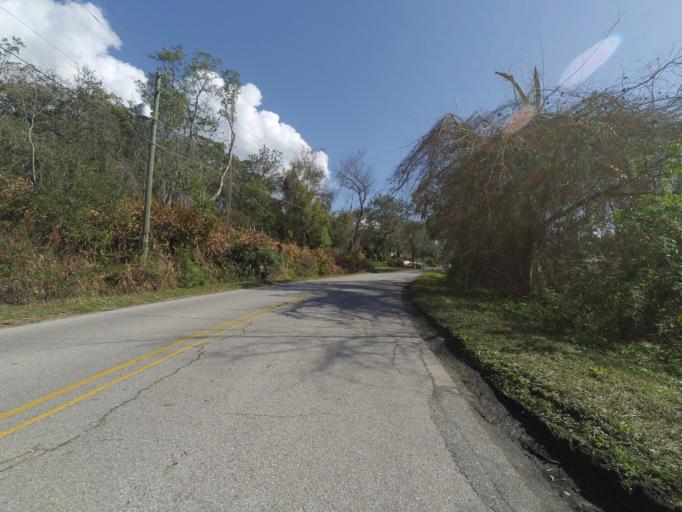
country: US
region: Florida
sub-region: Lake County
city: Mount Dora
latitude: 28.8197
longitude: -81.6516
